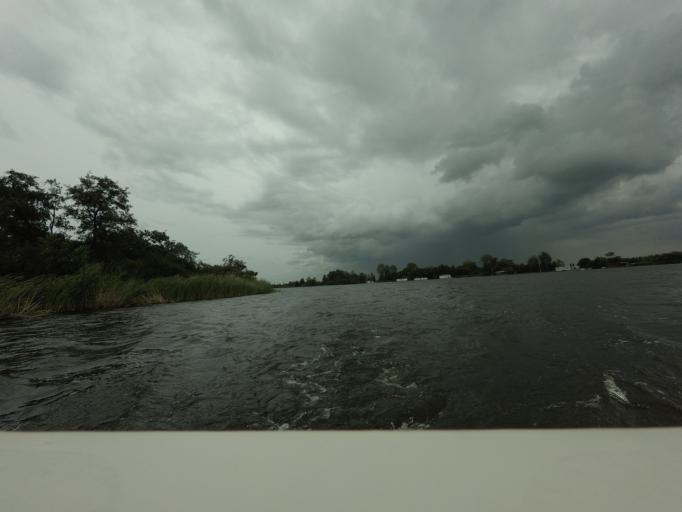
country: NL
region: Friesland
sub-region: Gemeente Boarnsterhim
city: Warten
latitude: 53.1185
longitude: 5.9432
